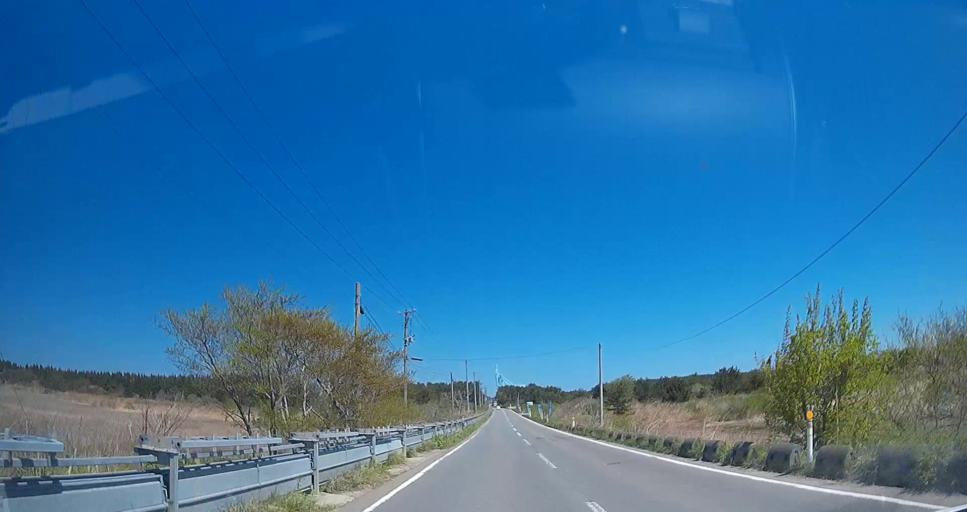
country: JP
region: Aomori
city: Misawa
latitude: 40.9325
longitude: 141.3750
